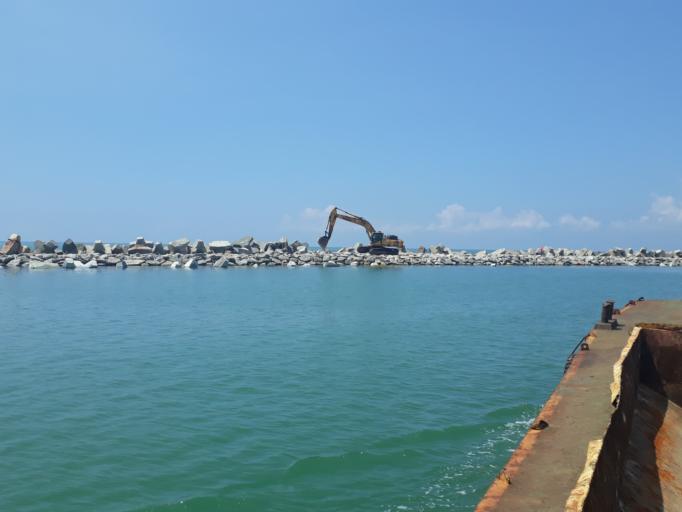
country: LK
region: Western
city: Colombo
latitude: 6.9239
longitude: 79.8311
